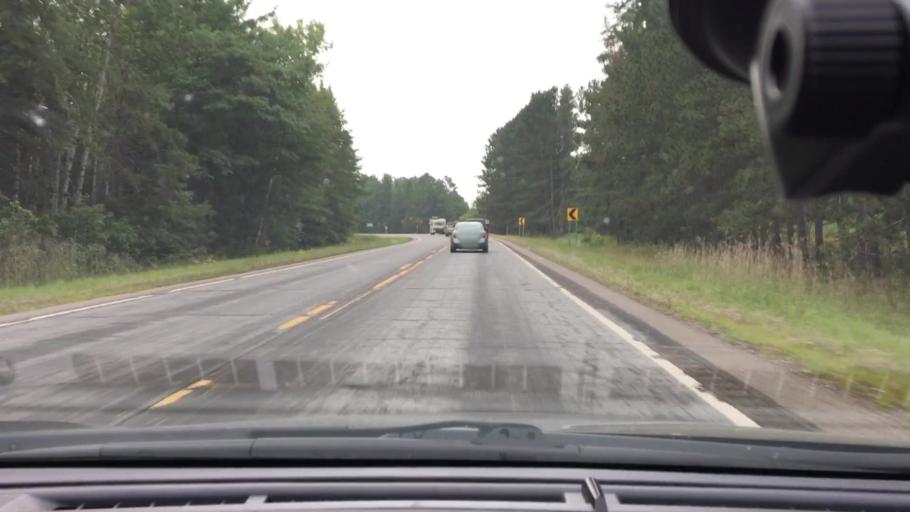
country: US
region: Minnesota
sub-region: Crow Wing County
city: Cross Lake
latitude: 46.7451
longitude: -93.9670
